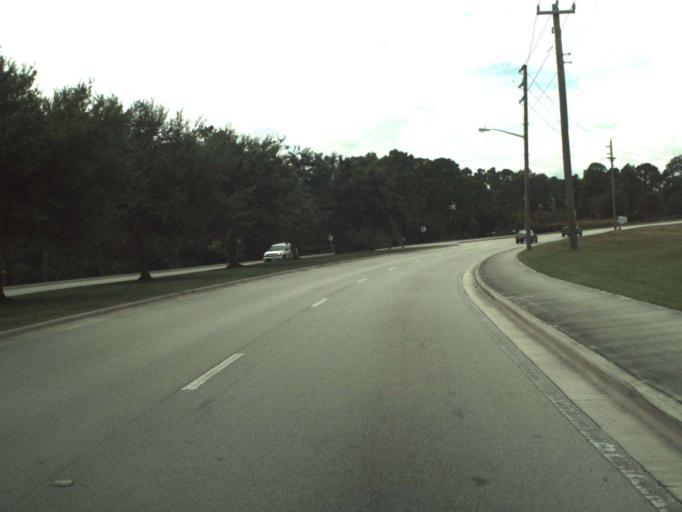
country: US
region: Florida
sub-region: Saint Lucie County
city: White City
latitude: 27.3659
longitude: -80.3505
